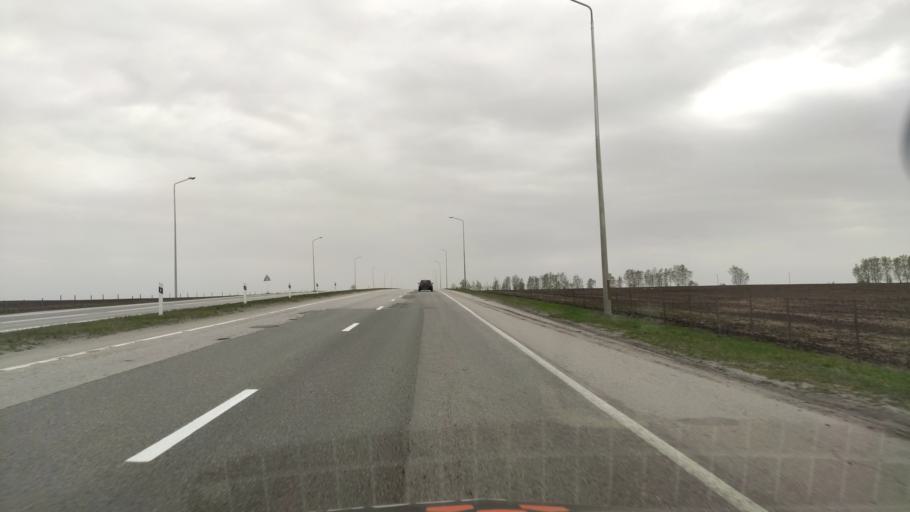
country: RU
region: Belgorod
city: Staryy Oskol
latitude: 51.3347
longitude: 37.7610
